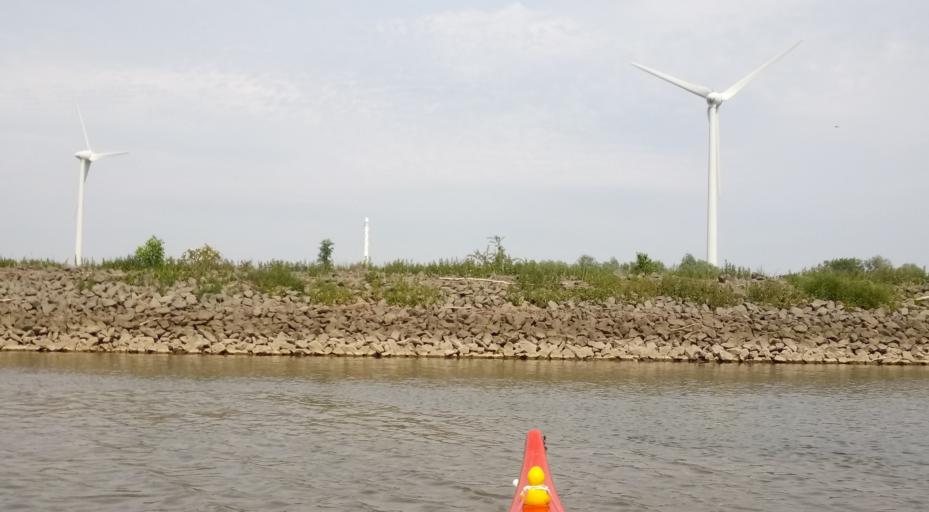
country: NL
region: Gelderland
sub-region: Gemeente Zutphen
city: Zutphen
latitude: 52.1583
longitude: 6.1854
